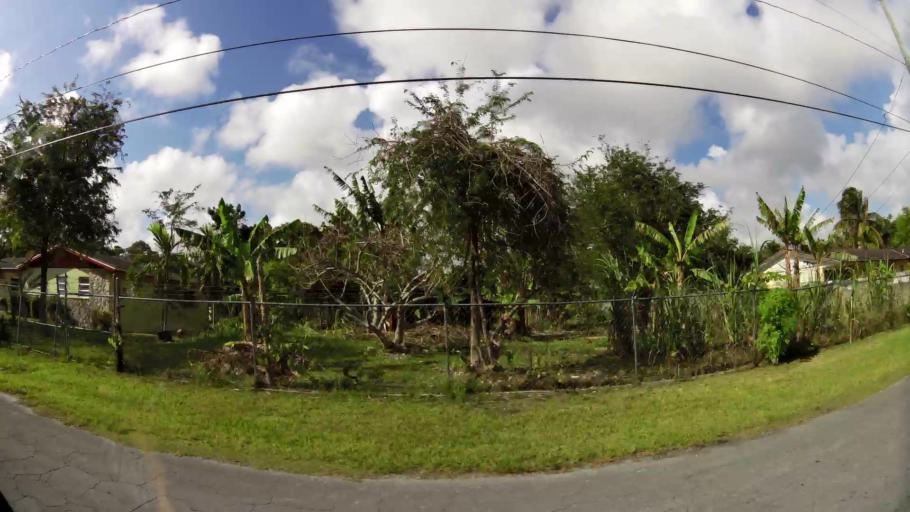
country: BS
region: Freeport
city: Freeport
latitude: 26.5234
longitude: -78.6841
